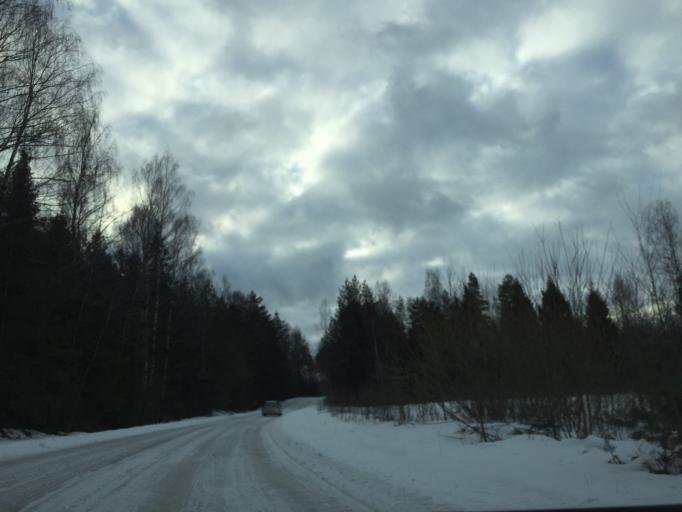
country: LV
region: Lielvarde
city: Lielvarde
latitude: 56.6223
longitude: 24.7750
